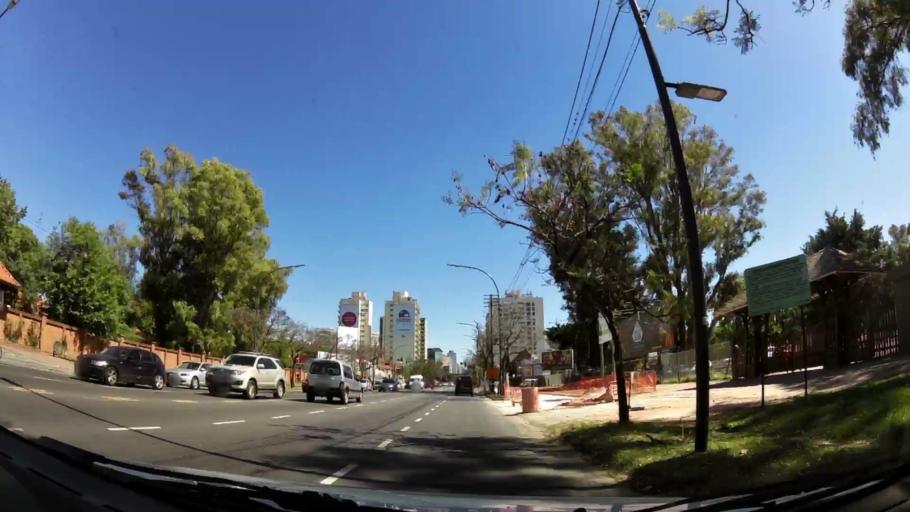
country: AR
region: Buenos Aires
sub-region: Partido de Vicente Lopez
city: Olivos
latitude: -34.5119
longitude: -58.4778
